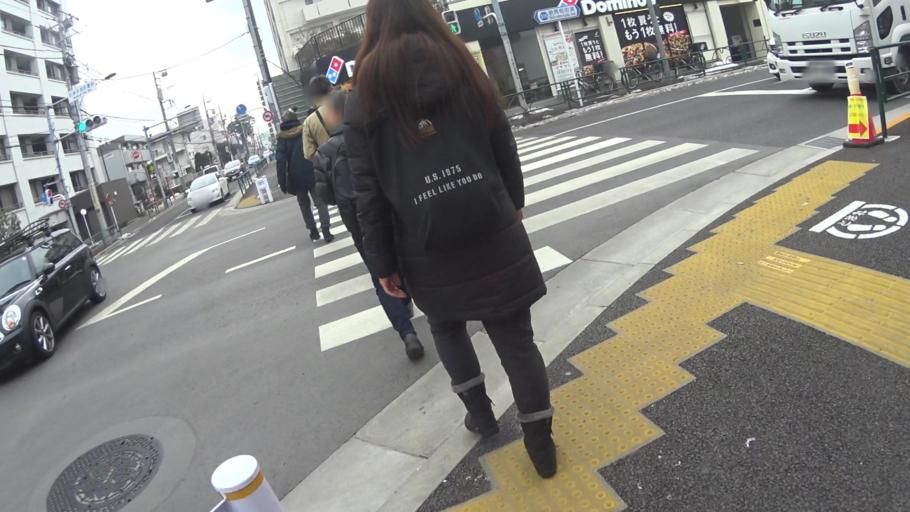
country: JP
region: Tokyo
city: Musashino
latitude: 35.7296
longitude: 139.5995
